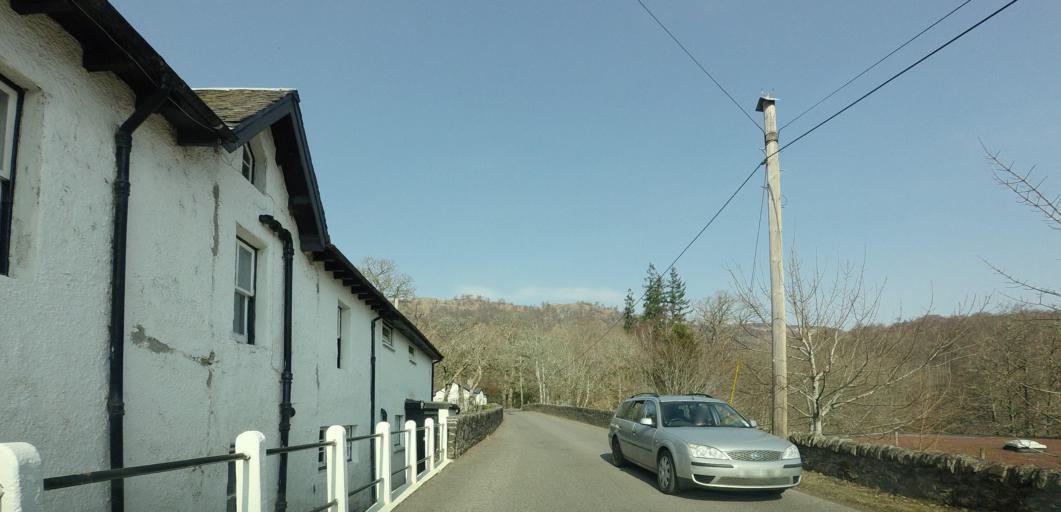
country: GB
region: Scotland
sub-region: Stirling
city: Callander
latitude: 56.4781
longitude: -4.3240
